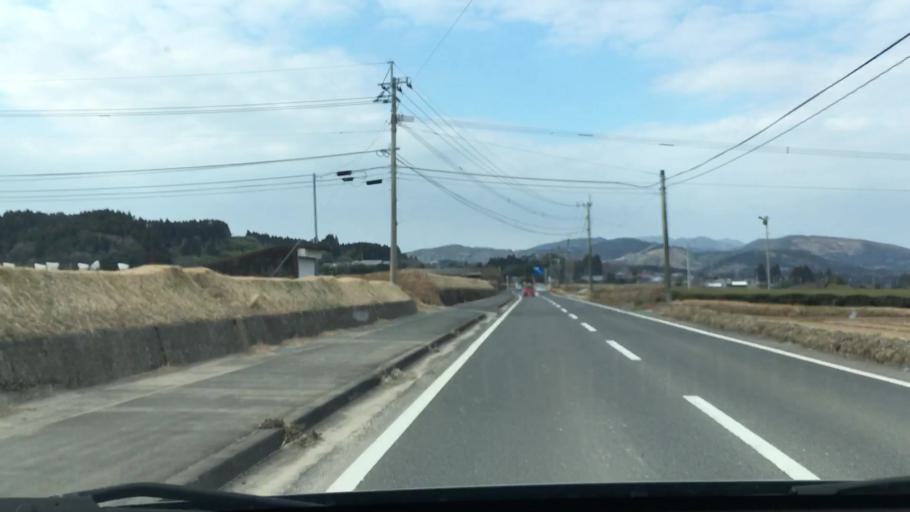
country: JP
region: Miyazaki
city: Kushima
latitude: 31.5168
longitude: 131.2390
